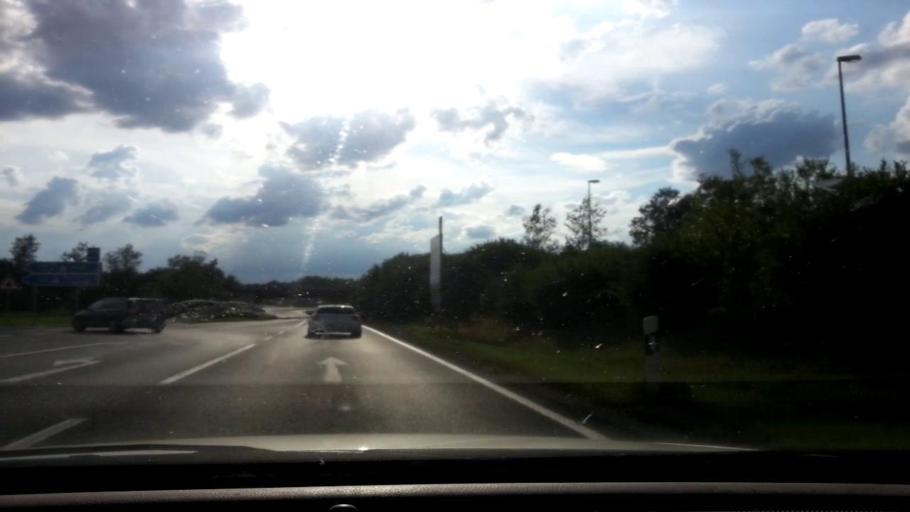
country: DE
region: Bavaria
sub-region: Upper Palatinate
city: Mitterteich
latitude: 49.9360
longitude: 12.2270
